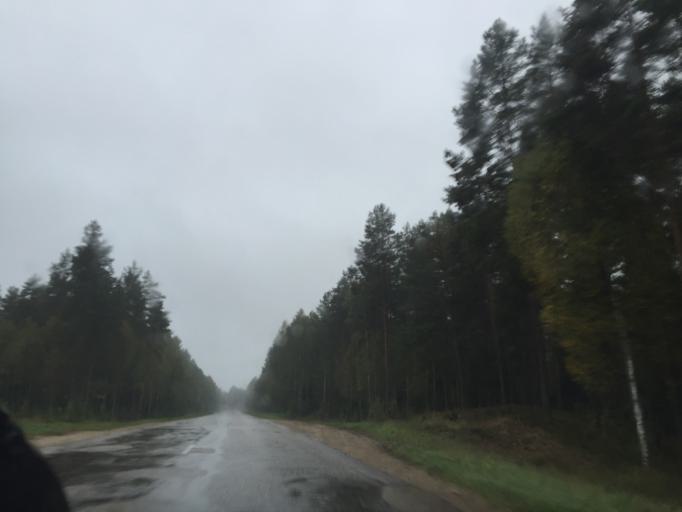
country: LV
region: Ropazu
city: Ropazi
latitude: 57.0048
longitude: 24.6735
